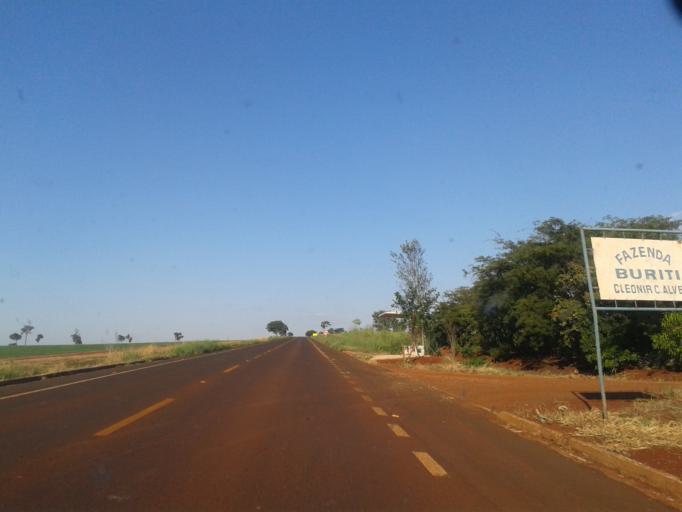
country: BR
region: Minas Gerais
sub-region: Capinopolis
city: Capinopolis
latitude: -18.7121
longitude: -49.8134
